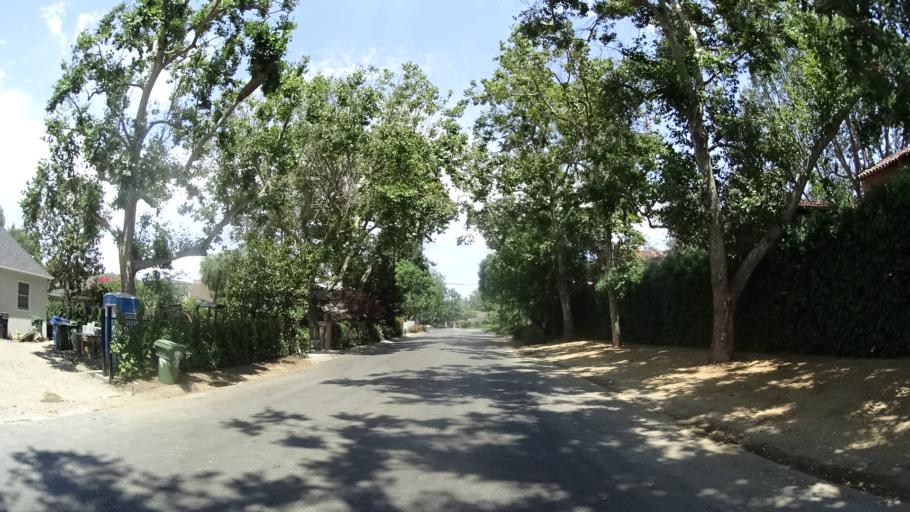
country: US
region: California
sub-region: Los Angeles County
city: Sherman Oaks
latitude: 34.1436
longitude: -118.4209
